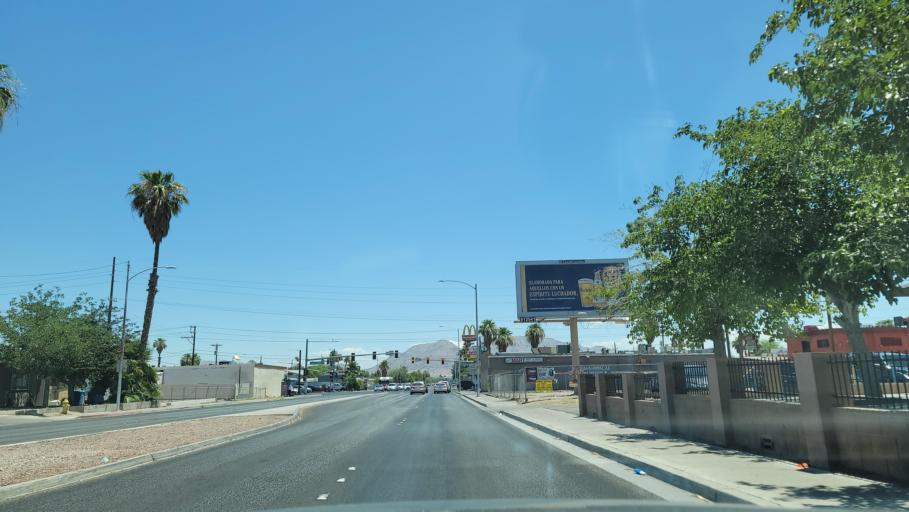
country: US
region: Nevada
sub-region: Clark County
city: North Las Vegas
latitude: 36.1884
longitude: -115.1177
